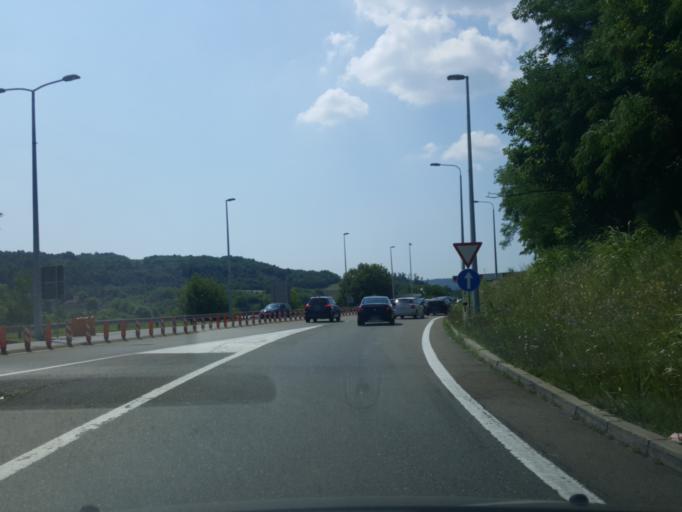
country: RS
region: Central Serbia
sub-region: Belgrade
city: Sopot
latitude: 44.5644
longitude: 20.6692
